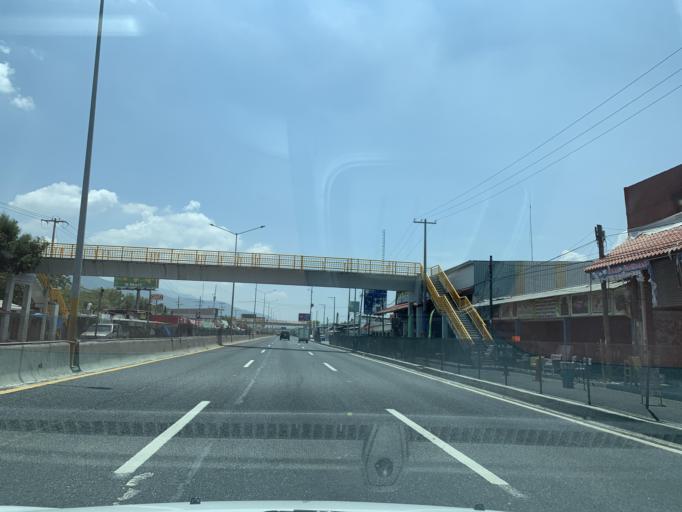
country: MX
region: Nuevo Leon
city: Santiago
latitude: 25.4520
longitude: -100.1632
